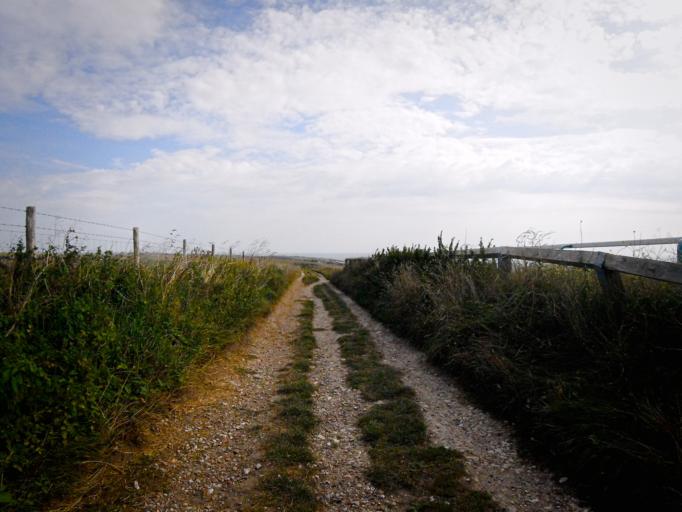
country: GB
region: England
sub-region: Brighton and Hove
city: Rottingdean
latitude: 50.8330
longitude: -0.0906
